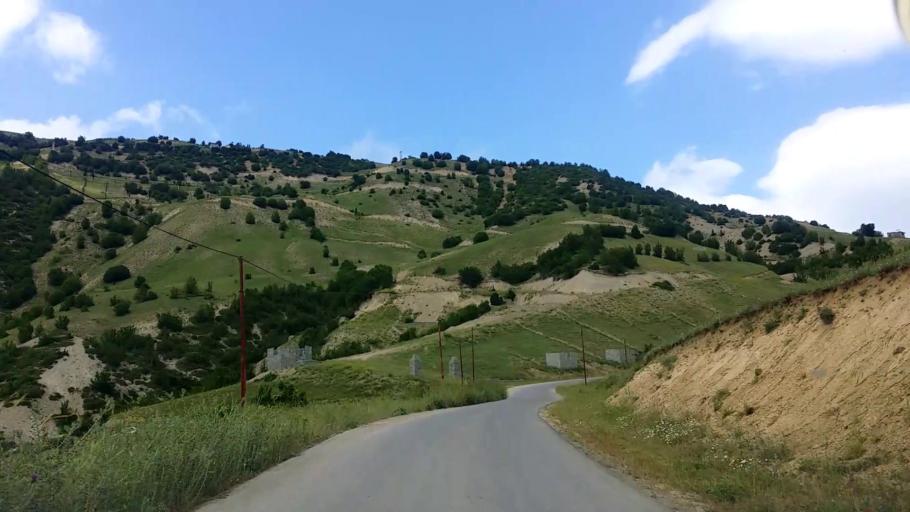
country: IR
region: Mazandaran
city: Chalus
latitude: 36.5523
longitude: 51.2803
